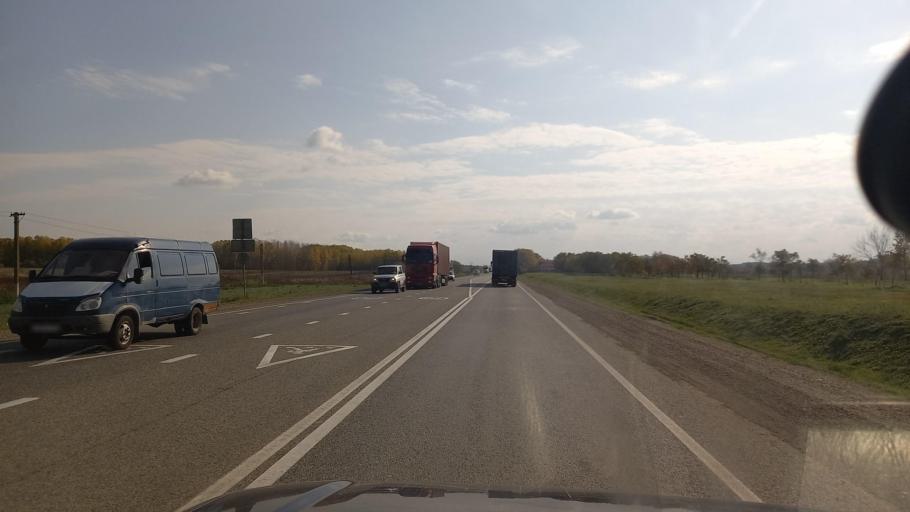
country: RU
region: Krasnodarskiy
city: Novoukrainskiy
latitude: 44.8888
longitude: 38.0769
